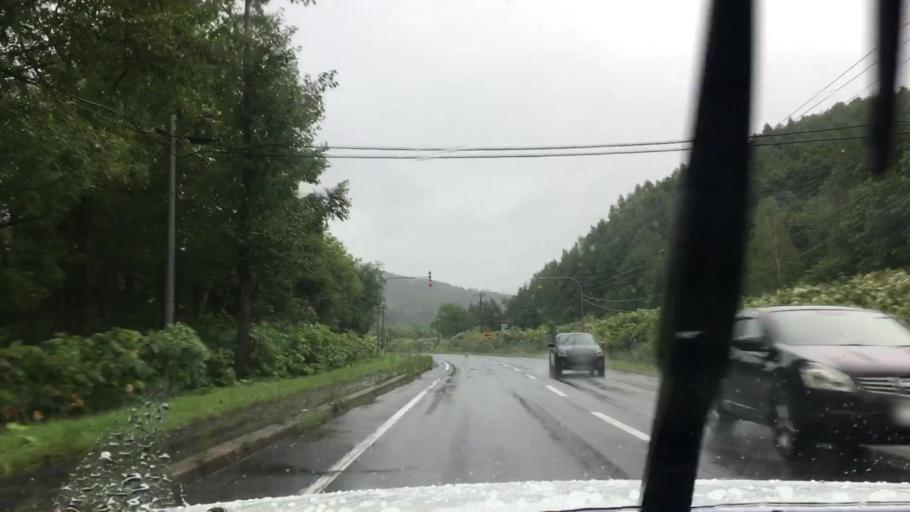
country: JP
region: Hokkaido
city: Niseko Town
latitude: 42.8046
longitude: 140.9935
